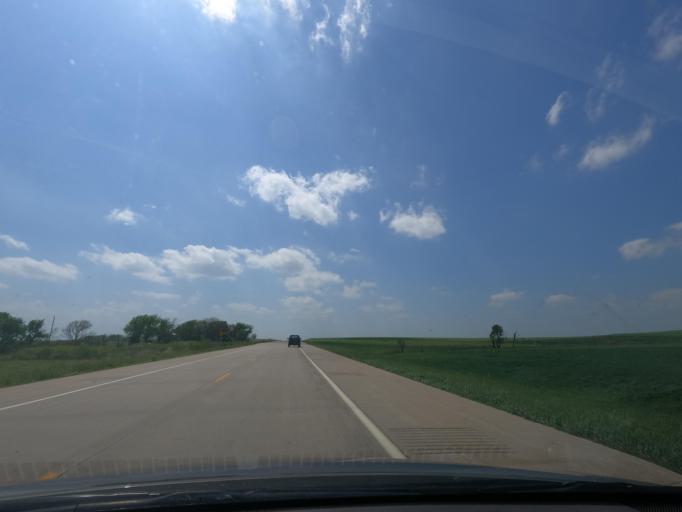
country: US
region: Kansas
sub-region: Elk County
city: Howard
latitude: 37.6279
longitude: -96.1144
